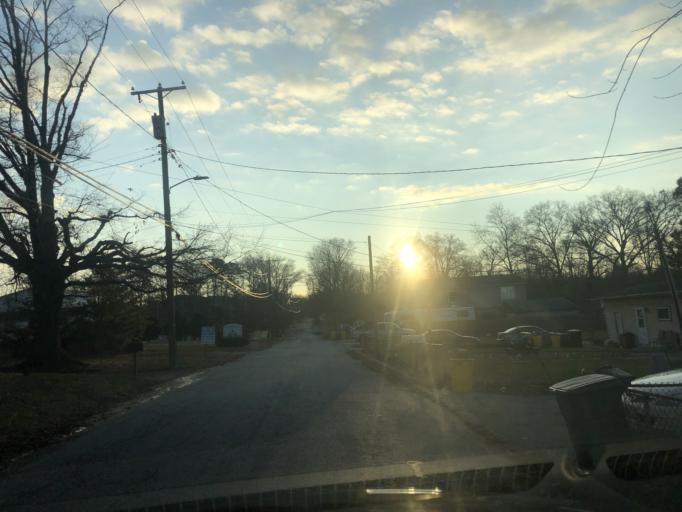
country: US
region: Maryland
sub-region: Anne Arundel County
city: Odenton
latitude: 39.0961
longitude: -76.7183
